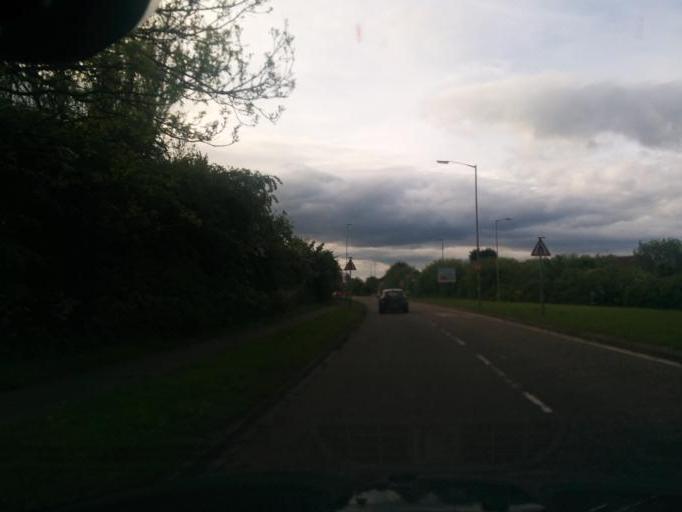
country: GB
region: England
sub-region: Northumberland
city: Bedlington
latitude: 55.1394
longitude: -1.5606
